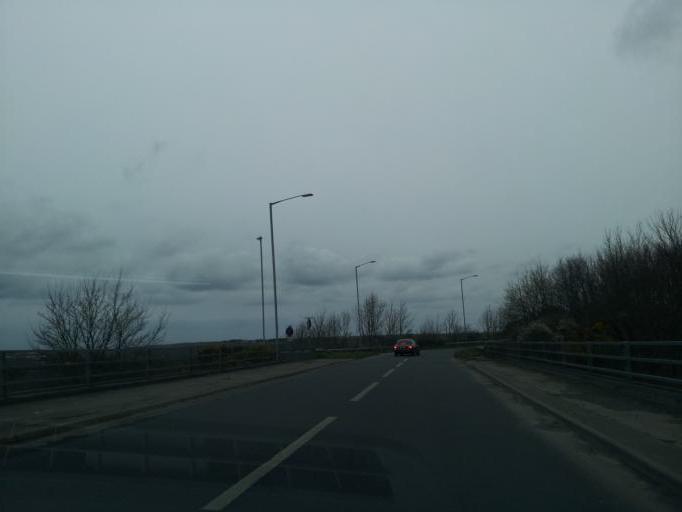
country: GB
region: England
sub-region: Cornwall
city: Redruth
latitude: 50.2432
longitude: -5.2342
